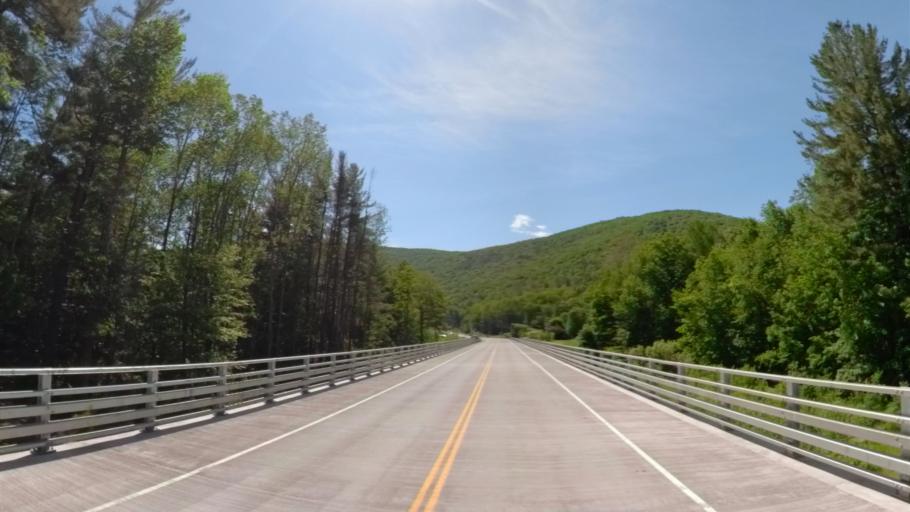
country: US
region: New York
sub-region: Ulster County
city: Shokan
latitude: 42.1046
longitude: -74.4466
